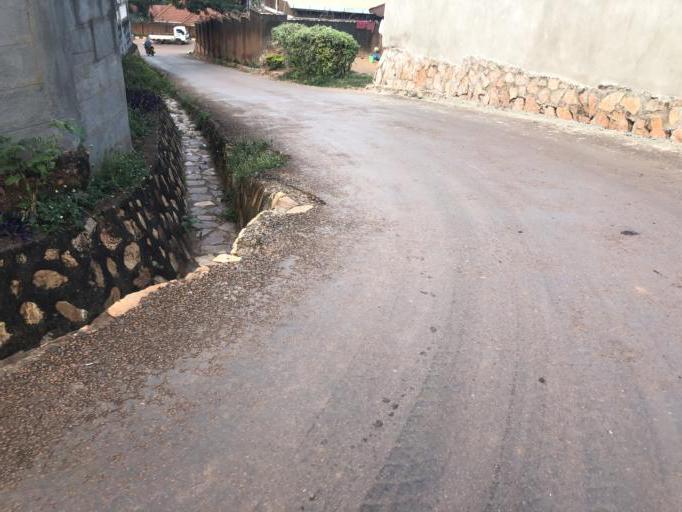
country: UG
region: Central Region
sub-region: Kampala District
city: Kampala
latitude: 0.2781
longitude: 32.5979
